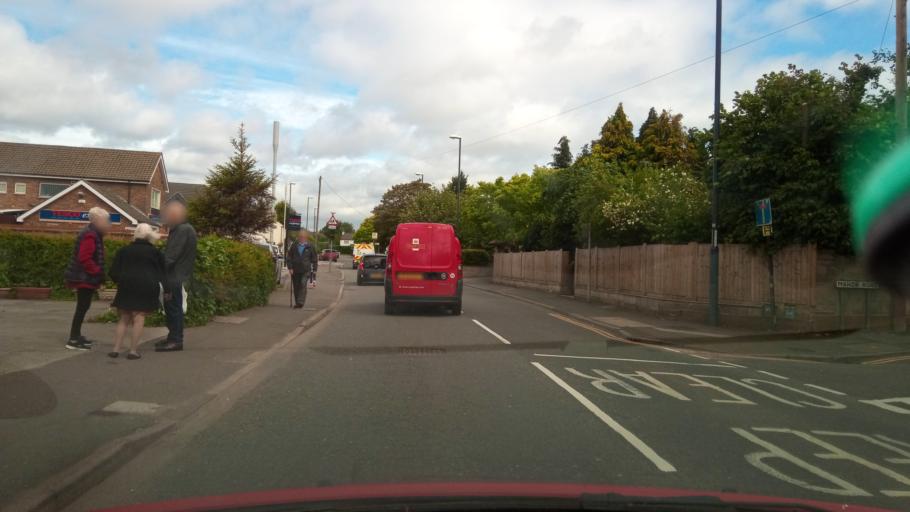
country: GB
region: England
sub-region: Derbyshire
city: Melbourne
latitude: 52.8694
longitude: -1.4388
